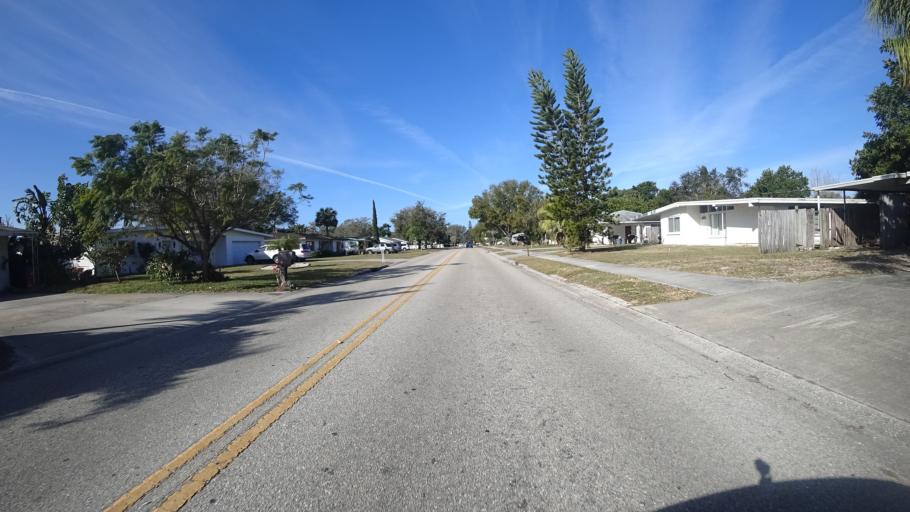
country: US
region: Florida
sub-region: Manatee County
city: West Bradenton
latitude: 27.4812
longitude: -82.6051
